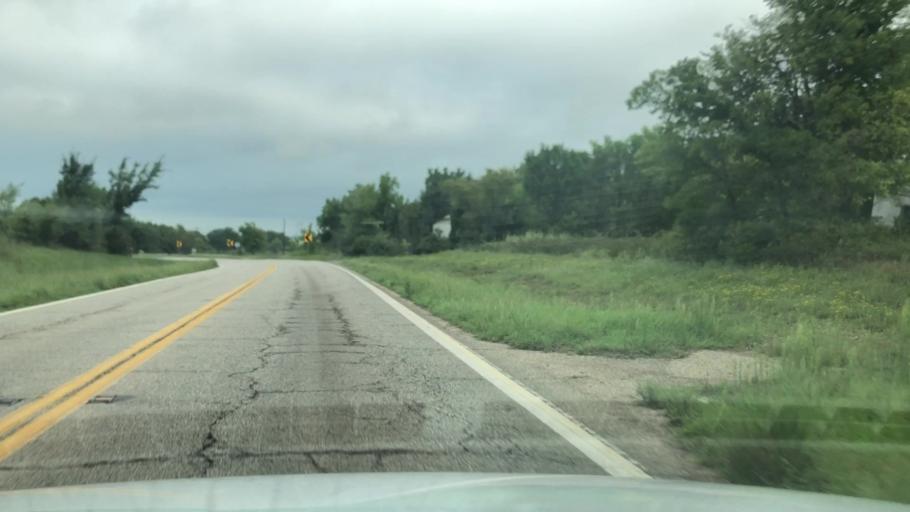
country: US
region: Oklahoma
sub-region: Nowata County
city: Nowata
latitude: 36.7127
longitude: -95.6624
